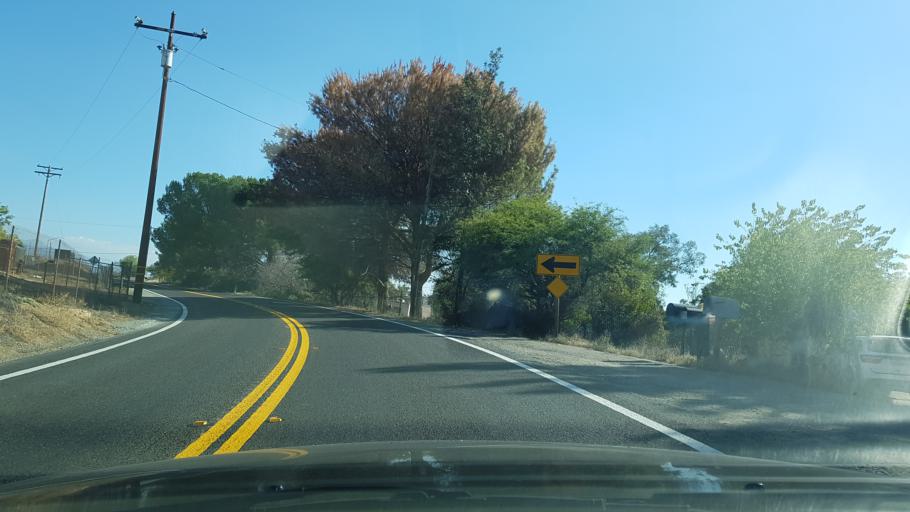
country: US
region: California
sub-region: San Diego County
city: San Diego Country Estates
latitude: 33.0812
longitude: -116.7846
